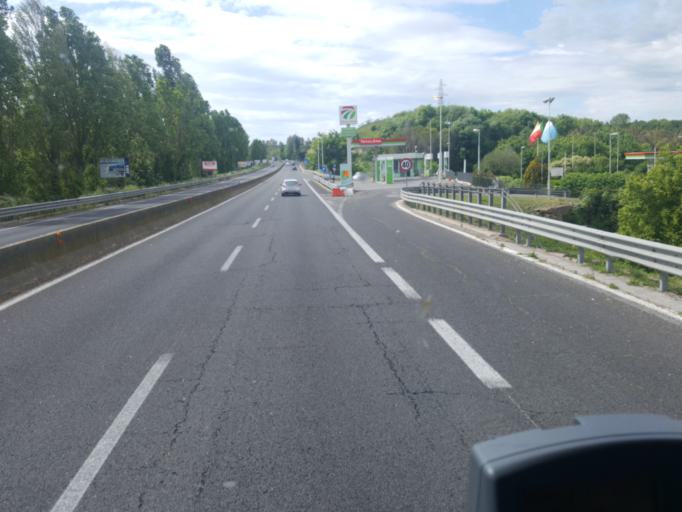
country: IT
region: Latium
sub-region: Citta metropolitana di Roma Capitale
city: Valle Santa
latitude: 41.8917
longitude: 12.2966
